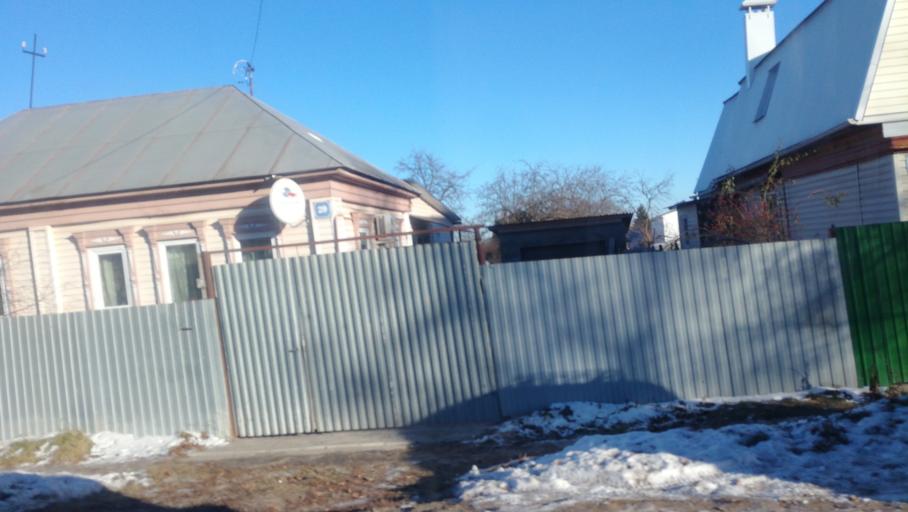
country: RU
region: Tula
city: Tula
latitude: 54.2016
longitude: 37.5571
